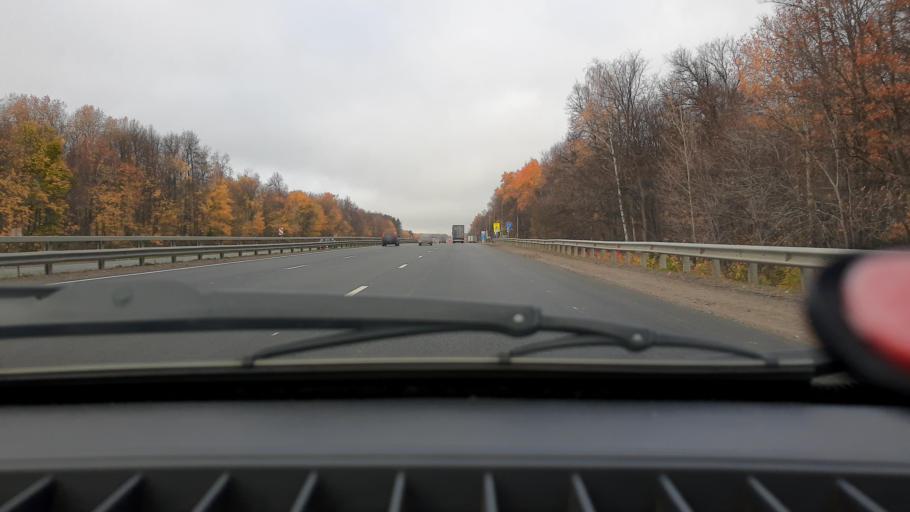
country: RU
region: Bashkortostan
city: Avdon
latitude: 54.6629
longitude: 55.7229
